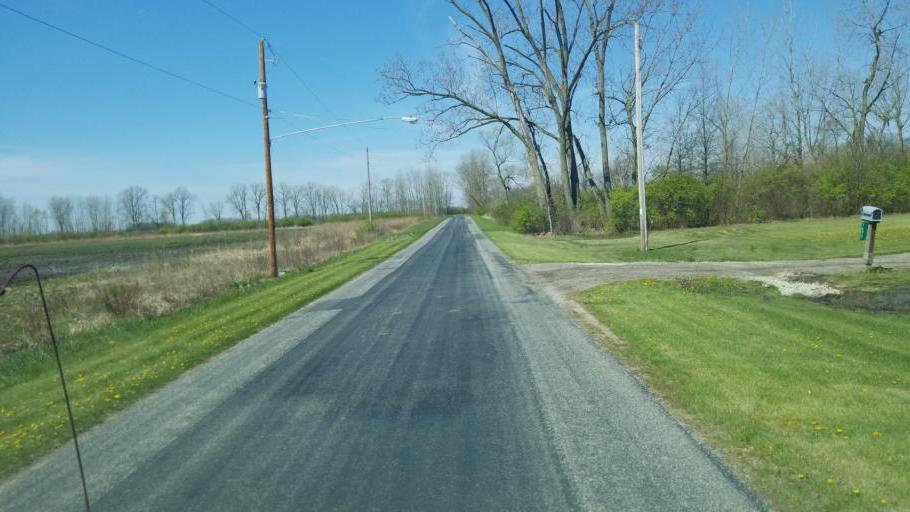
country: US
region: Ohio
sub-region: Marion County
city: Marion
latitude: 40.6426
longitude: -83.0881
